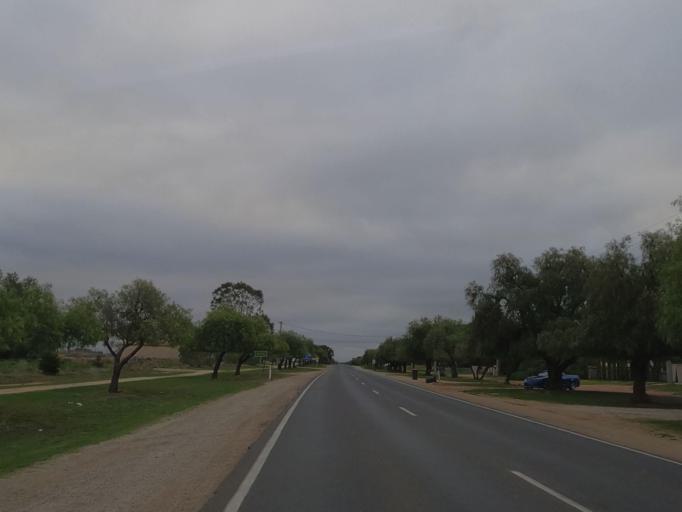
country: AU
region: Victoria
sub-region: Swan Hill
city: Swan Hill
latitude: -35.4570
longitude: 143.6300
